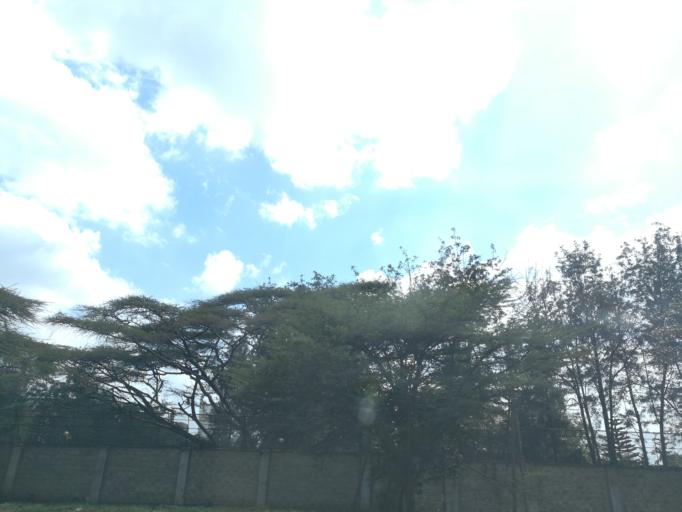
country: KE
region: Nairobi Area
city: Nairobi
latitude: -1.2993
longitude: 36.7946
